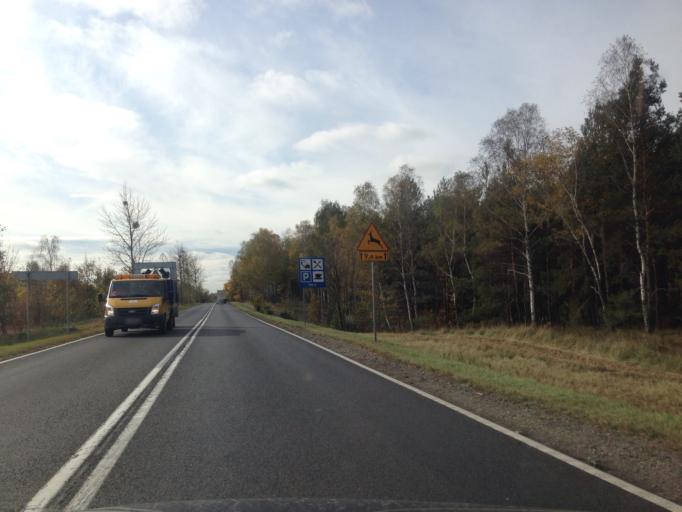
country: PL
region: Kujawsko-Pomorskie
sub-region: Powiat brodnicki
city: Brzozie
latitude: 53.3201
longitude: 19.5324
